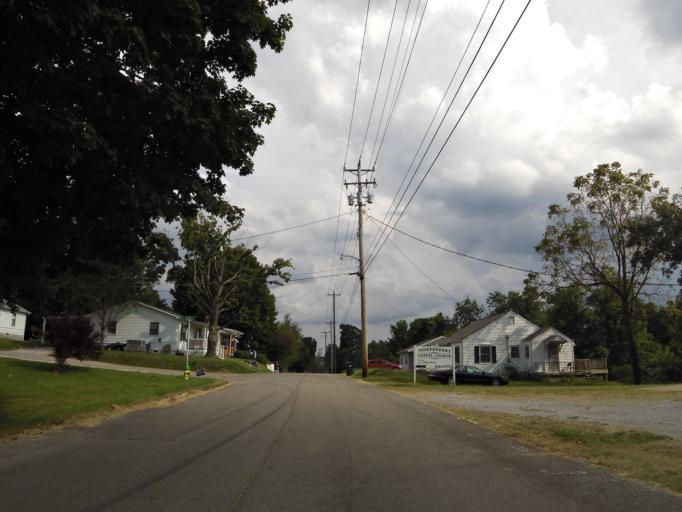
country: US
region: Tennessee
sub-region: Dickson County
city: Dickson
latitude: 36.0793
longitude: -87.3923
